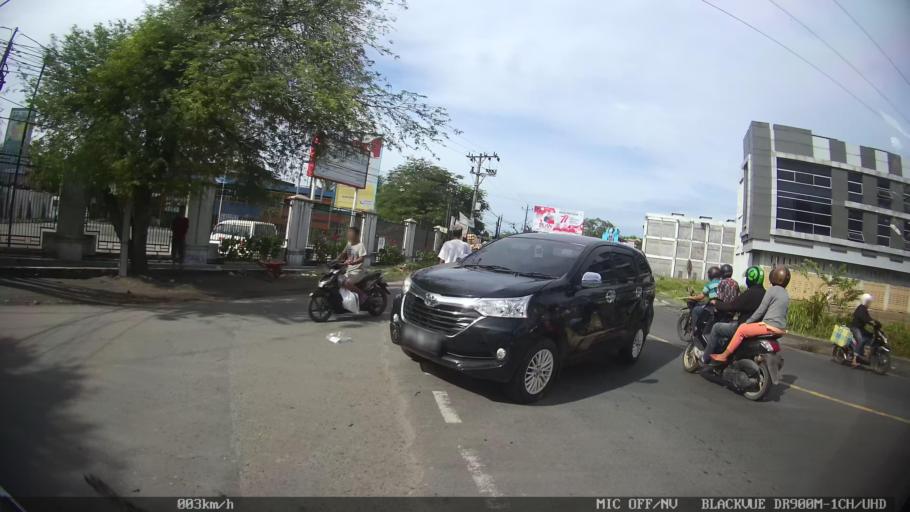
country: ID
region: North Sumatra
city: Medan
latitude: 3.6229
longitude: 98.6601
